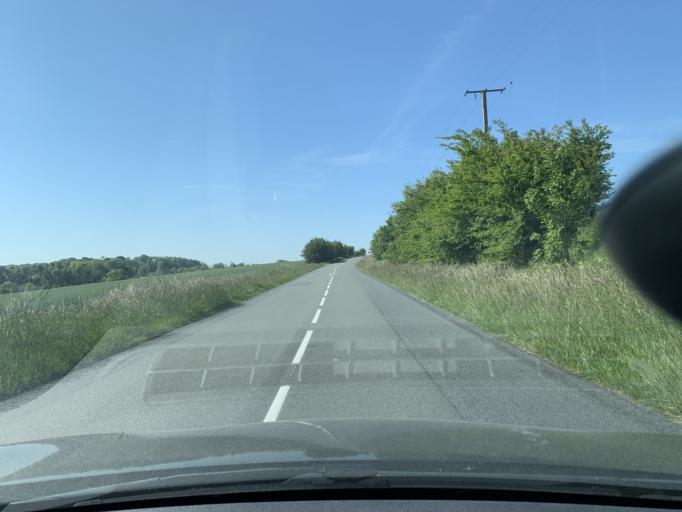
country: FR
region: Nord-Pas-de-Calais
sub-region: Departement du Nord
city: Masnieres
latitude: 50.0825
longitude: 3.2172
